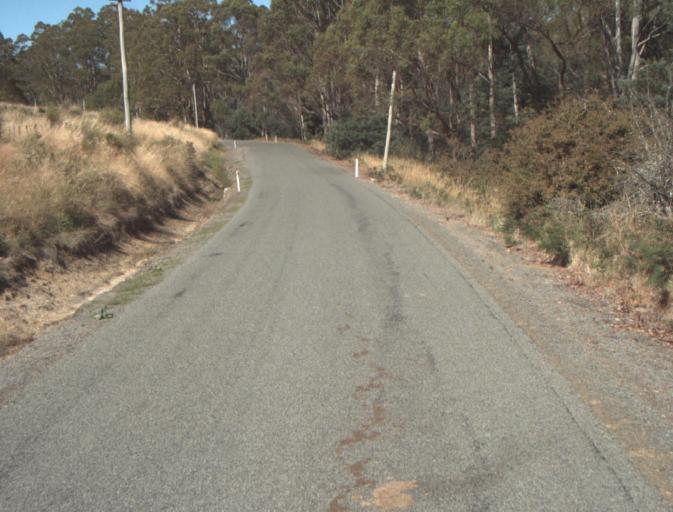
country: AU
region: Tasmania
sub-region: Launceston
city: Newstead
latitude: -41.3589
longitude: 147.3024
